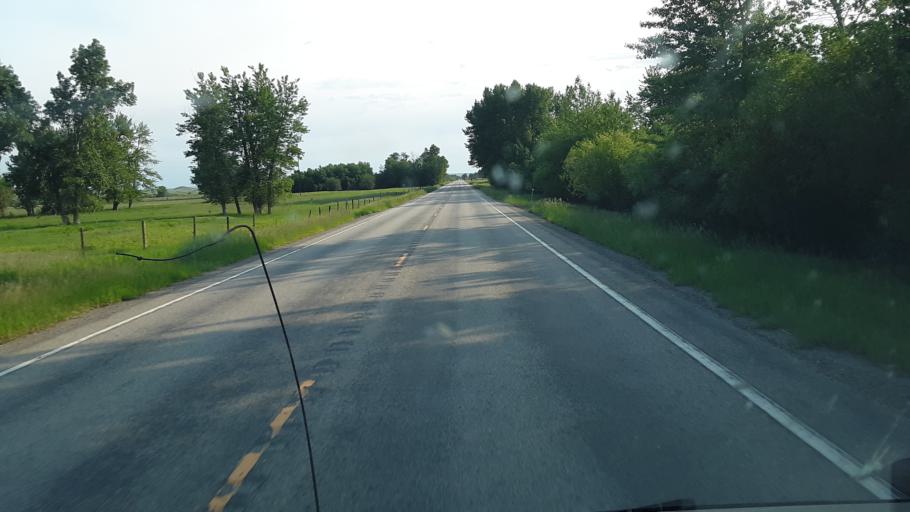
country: US
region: Montana
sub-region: Carbon County
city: Red Lodge
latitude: 45.3231
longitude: -109.1899
